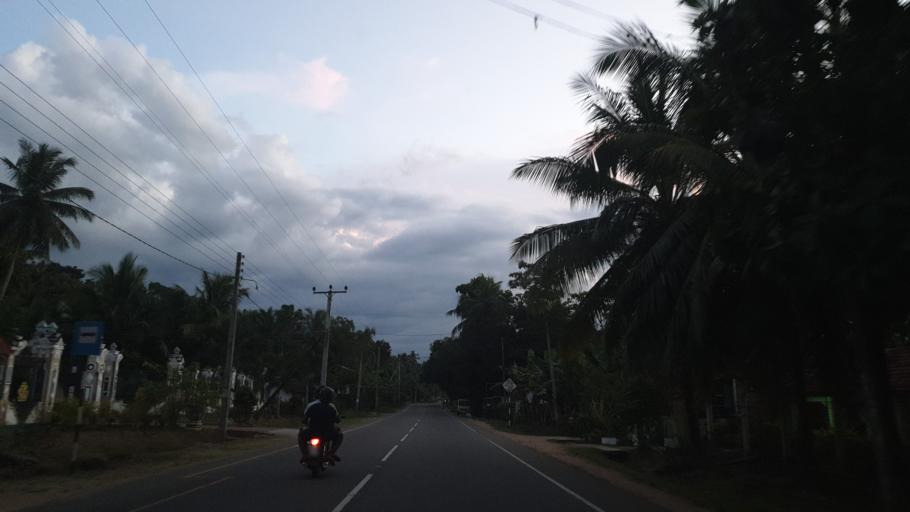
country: LK
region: North Western
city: Kurunegala
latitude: 7.5867
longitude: 80.2003
